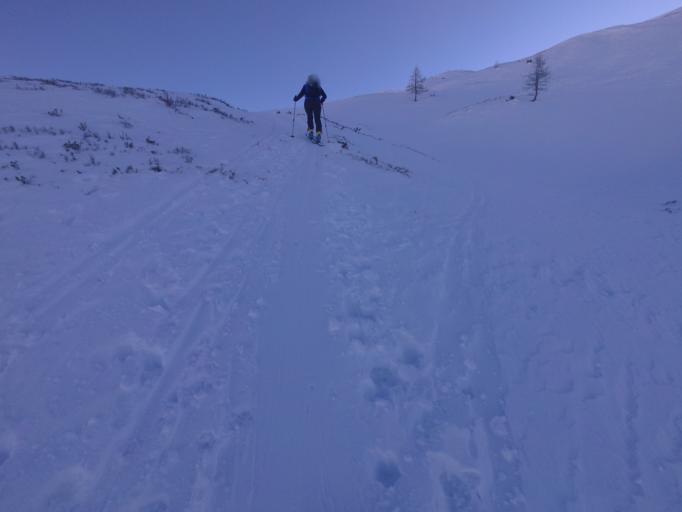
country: AT
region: Salzburg
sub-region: Politischer Bezirk Sankt Johann im Pongau
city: Huttschlag
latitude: 47.1751
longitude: 13.3003
